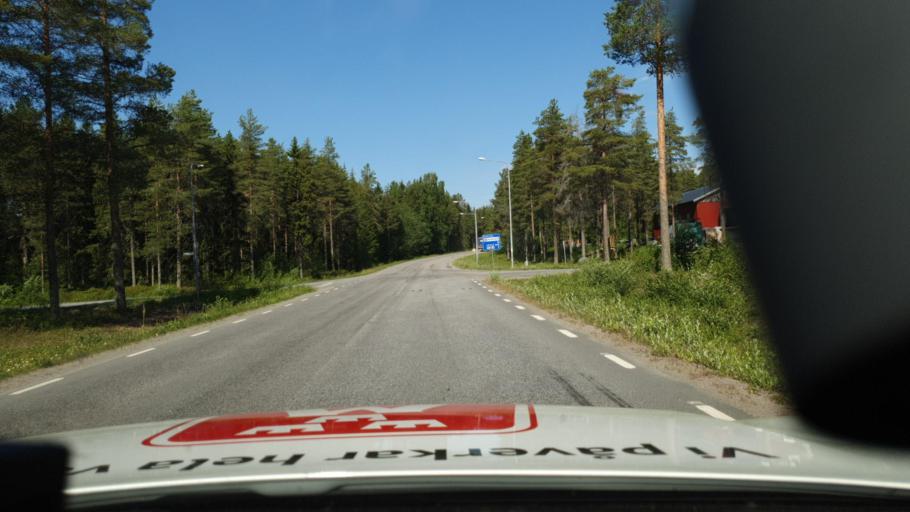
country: SE
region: Norrbotten
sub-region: Lulea Kommun
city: Ranea
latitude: 65.8622
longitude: 22.3135
